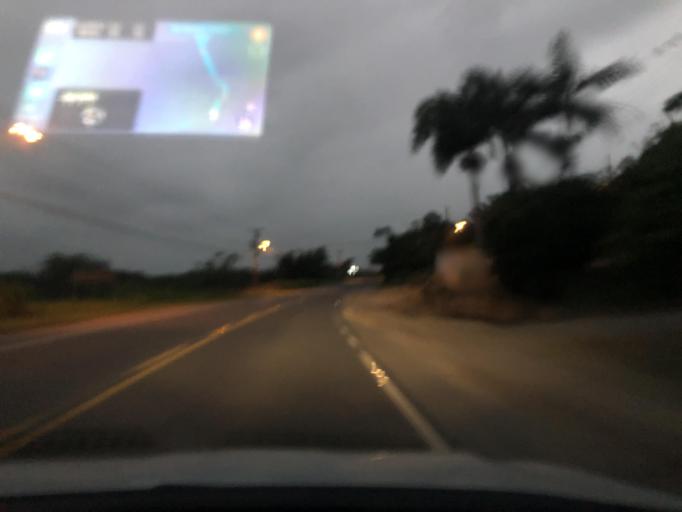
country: BR
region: Santa Catarina
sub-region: Guaramirim
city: Guaramirim
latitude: -26.6002
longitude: -49.0033
